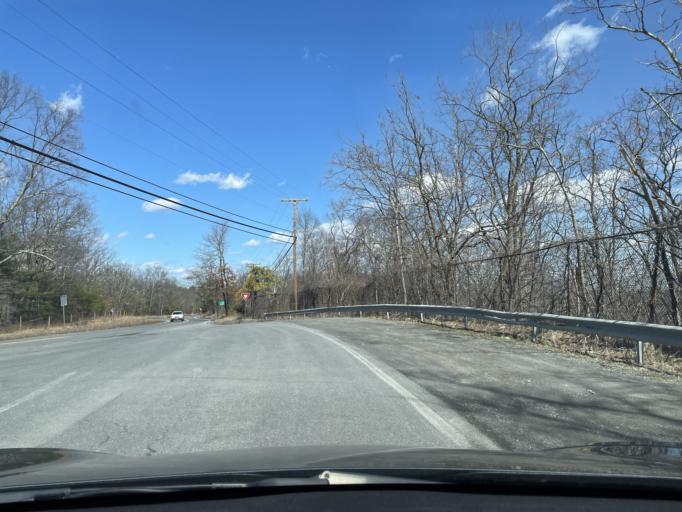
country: US
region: New York
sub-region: Ulster County
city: West Hurley
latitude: 41.9727
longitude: -74.1031
